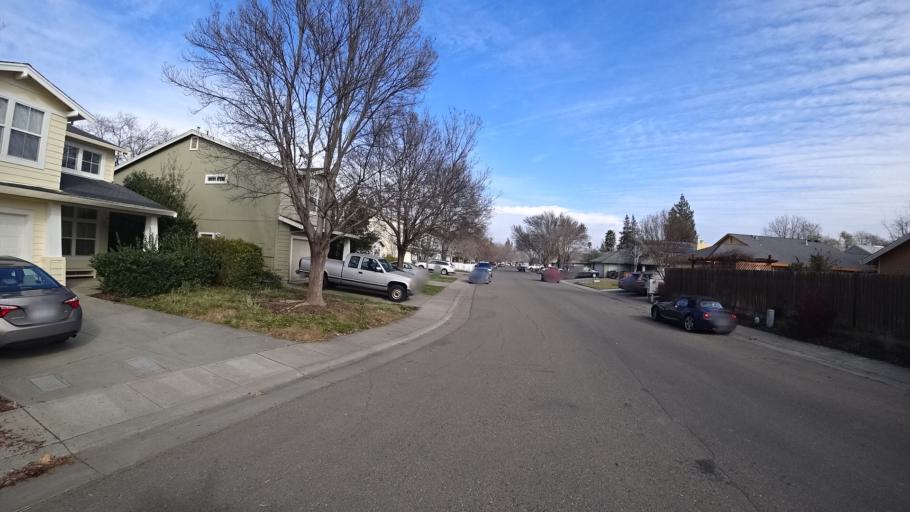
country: US
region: California
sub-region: Yolo County
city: Davis
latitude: 38.5454
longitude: -121.7206
